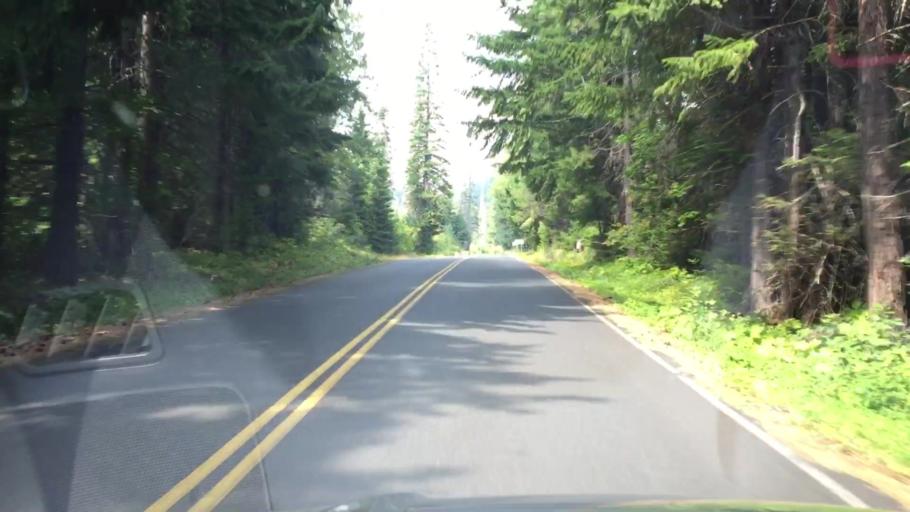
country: US
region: Washington
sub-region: Klickitat County
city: White Salmon
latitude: 46.0423
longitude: -121.5521
